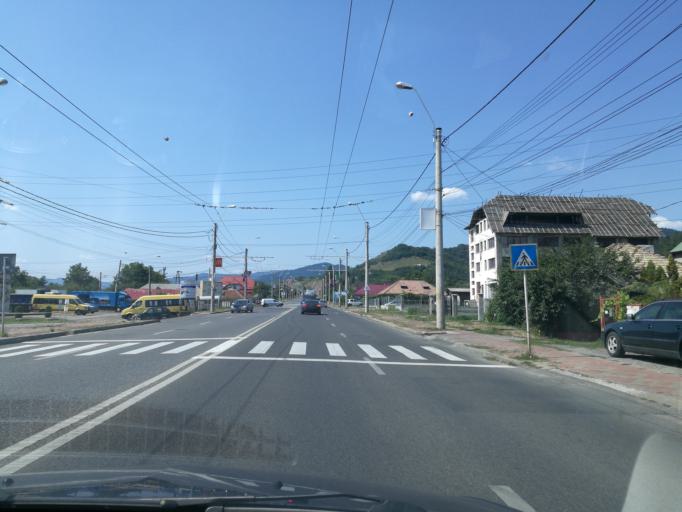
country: RO
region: Neamt
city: Piatra Neamt
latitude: 46.9385
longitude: 26.3392
